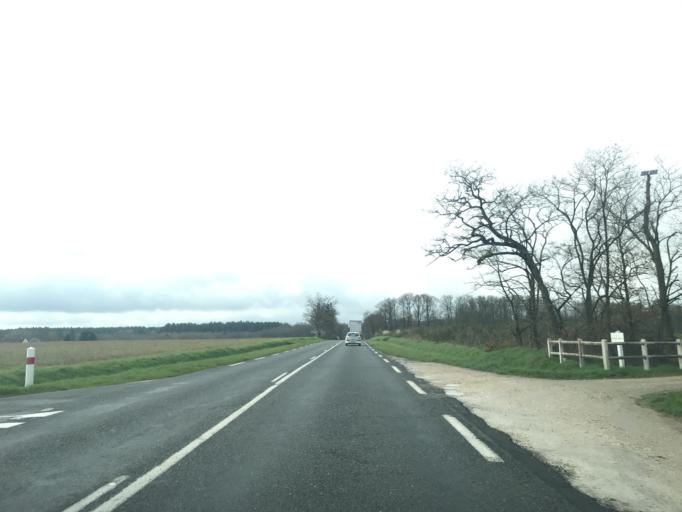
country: FR
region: Centre
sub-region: Departement du Loiret
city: Nevoy
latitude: 47.7230
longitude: 2.5808
